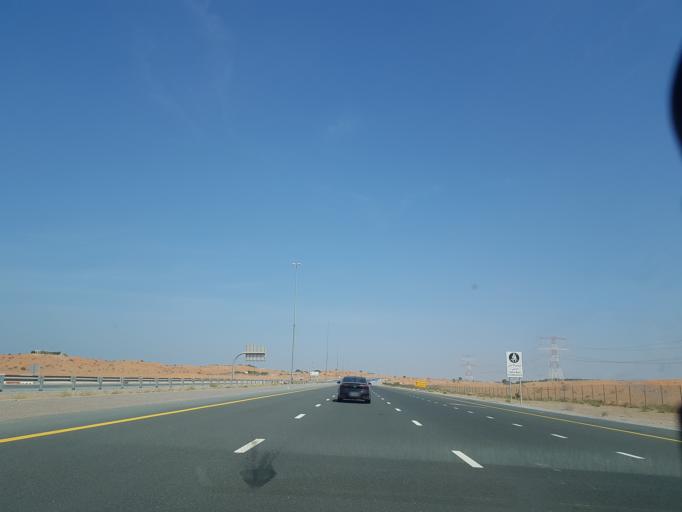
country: AE
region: Ra's al Khaymah
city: Ras al-Khaimah
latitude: 25.6665
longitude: 55.8958
